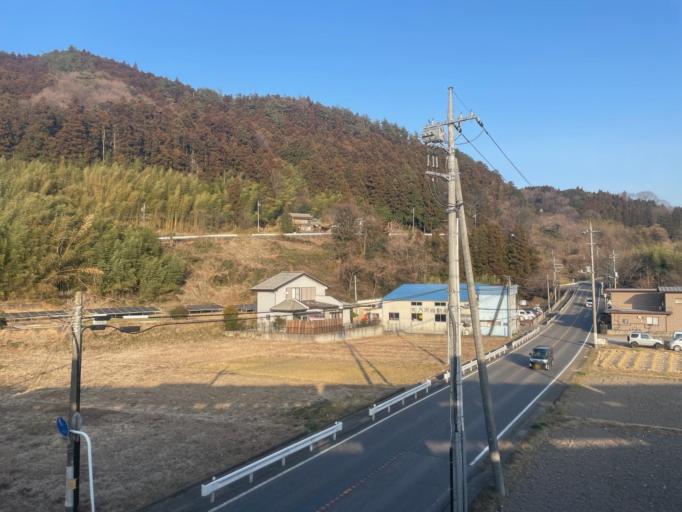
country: JP
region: Gunma
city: Shibukawa
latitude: 36.5472
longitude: 138.9555
